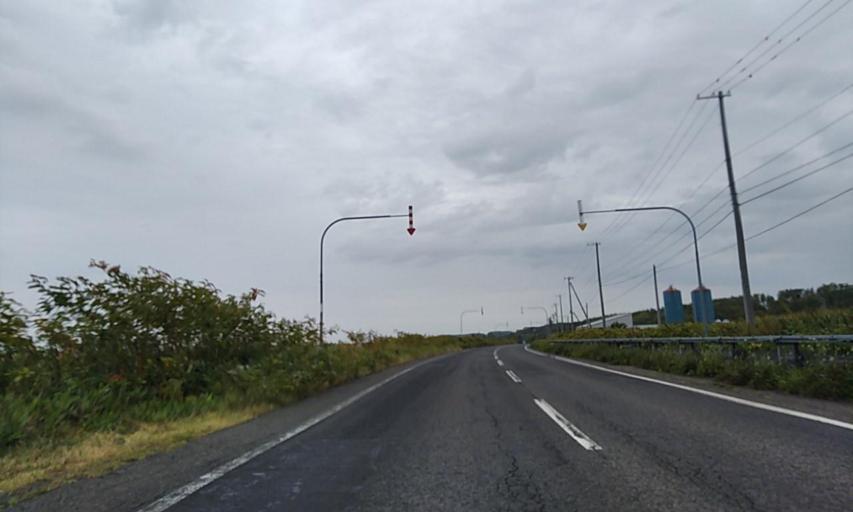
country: JP
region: Hokkaido
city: Mombetsu
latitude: 44.5382
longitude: 143.0258
